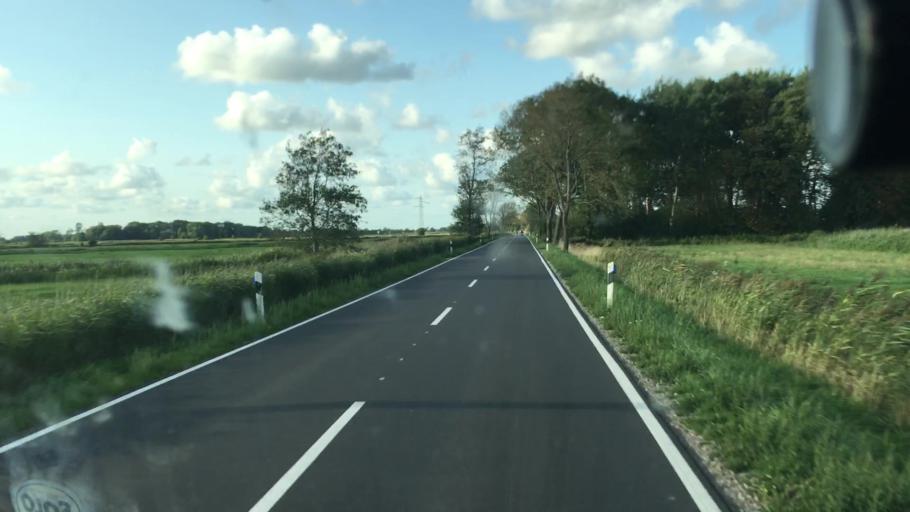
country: DE
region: Lower Saxony
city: Jever
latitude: 53.6315
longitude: 7.8615
